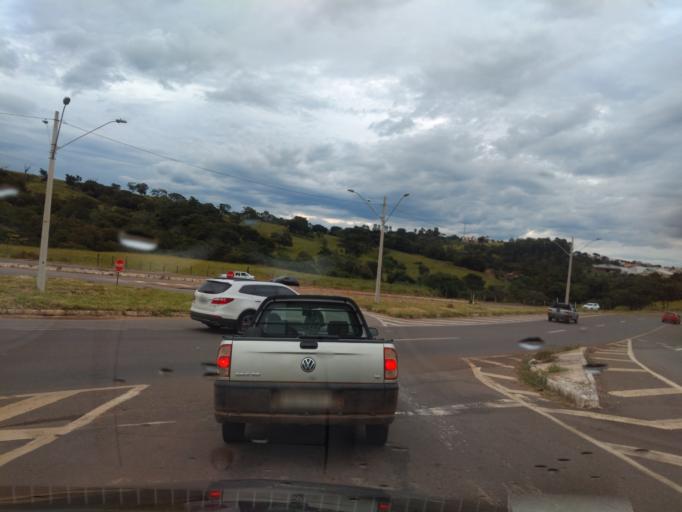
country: BR
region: Minas Gerais
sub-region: Varginha
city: Varginha
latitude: -21.5682
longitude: -45.4513
